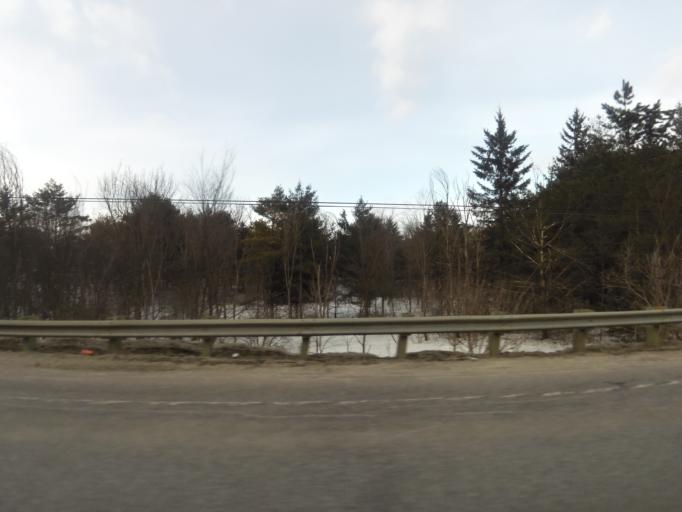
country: CA
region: Quebec
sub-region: Outaouais
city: Wakefield
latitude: 45.7691
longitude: -75.9390
